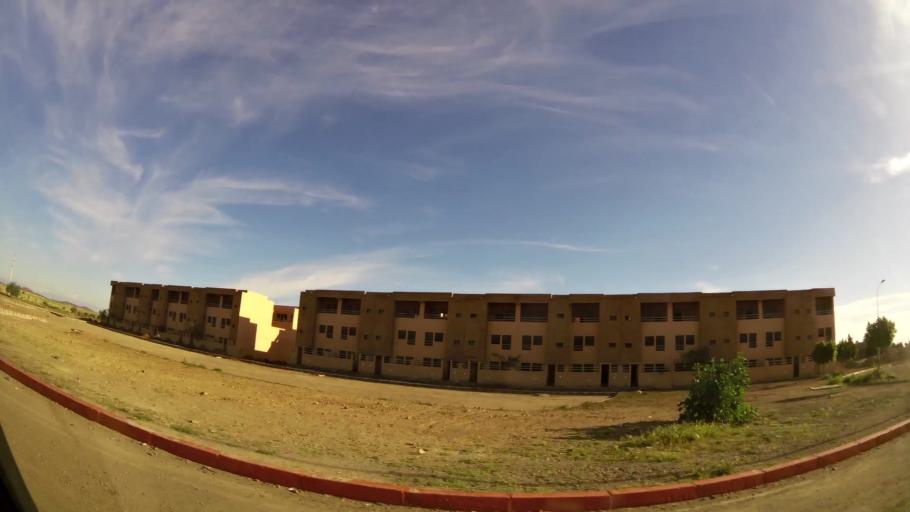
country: MA
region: Marrakech-Tensift-Al Haouz
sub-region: Marrakech
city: Marrakesh
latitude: 31.7539
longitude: -8.0958
